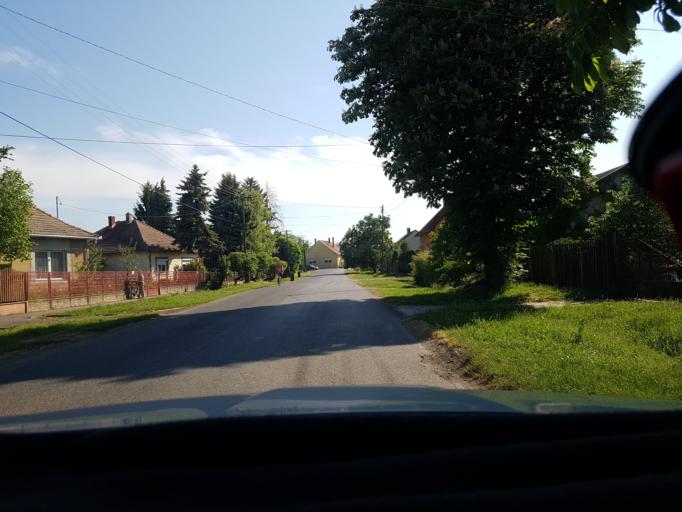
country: HU
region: Tolna
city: Decs
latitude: 46.2879
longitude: 18.7591
